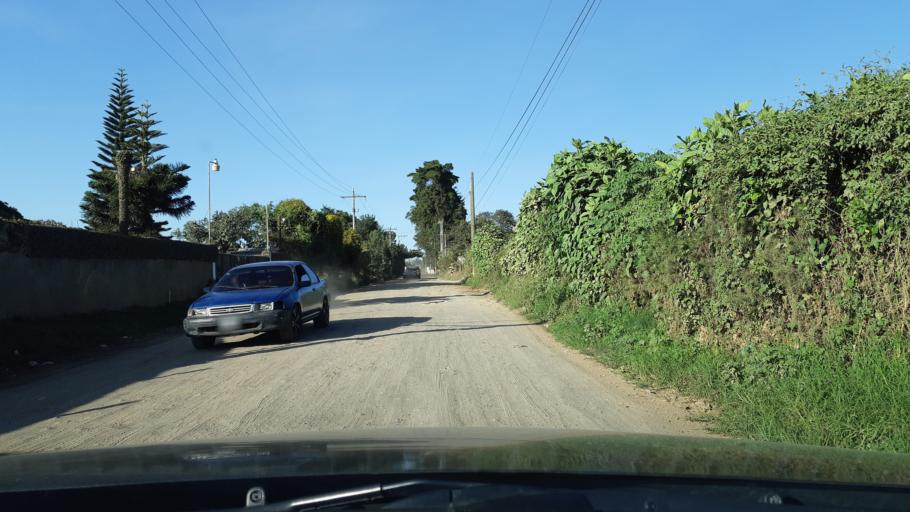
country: GT
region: Chimaltenango
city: El Tejar
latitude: 14.6379
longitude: -90.7997
